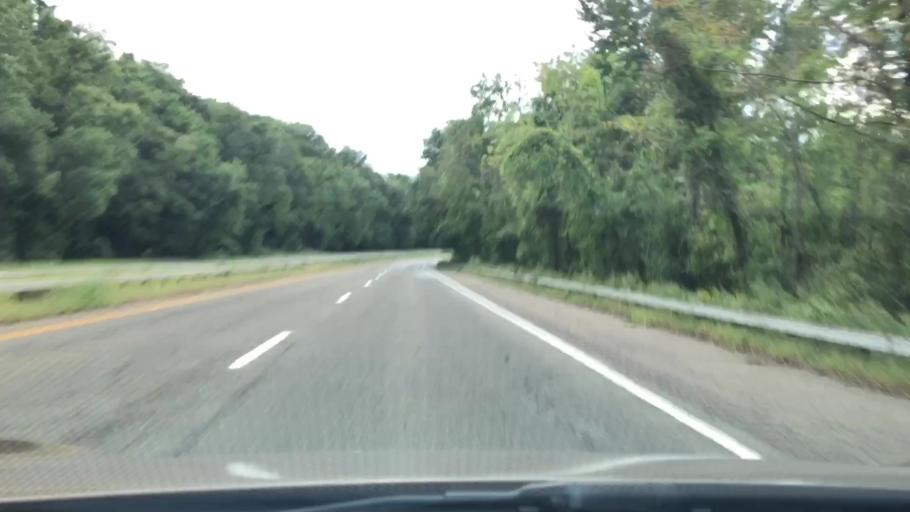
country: US
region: New York
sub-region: Westchester County
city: Sleepy Hollow
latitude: 41.1105
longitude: -73.8418
